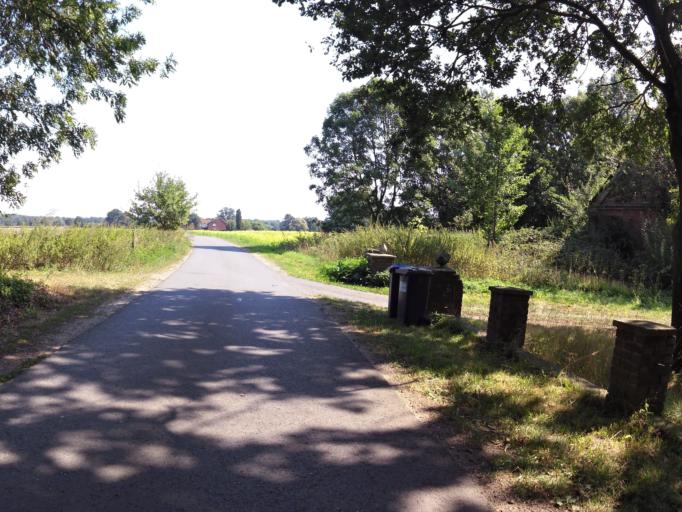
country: DE
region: North Rhine-Westphalia
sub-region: Regierungsbezirk Munster
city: Telgte
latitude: 51.9625
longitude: 7.7155
